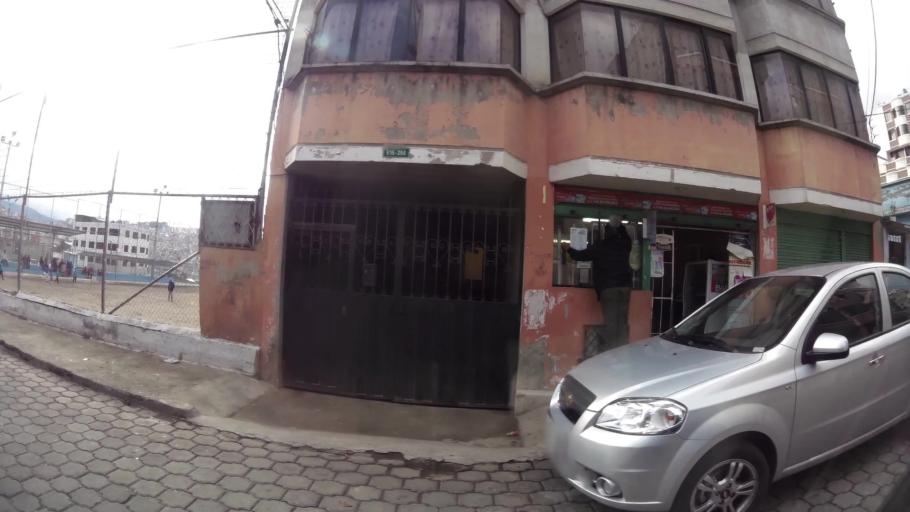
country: EC
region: Pichincha
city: Quito
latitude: -0.1281
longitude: -78.4621
